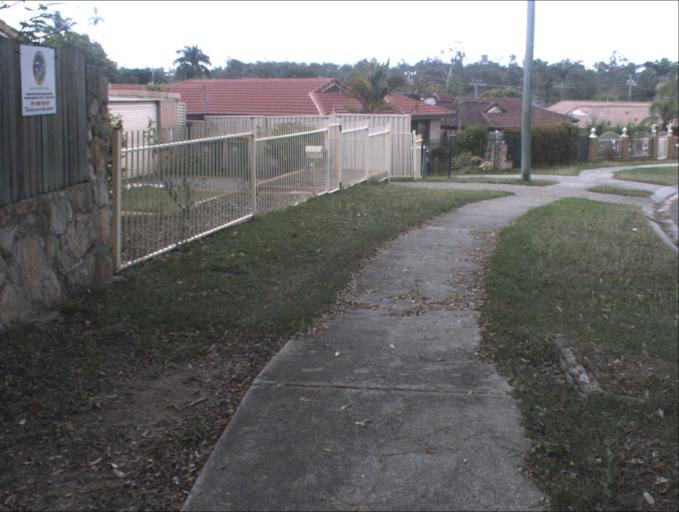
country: AU
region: Queensland
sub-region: Logan
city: Park Ridge South
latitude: -27.6948
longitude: 153.0203
